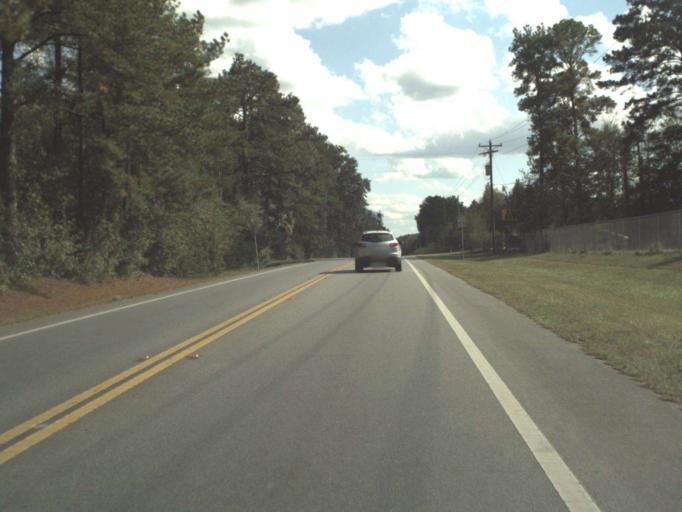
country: US
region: Florida
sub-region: Gadsden County
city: Gretna
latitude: 30.6045
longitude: -84.6545
